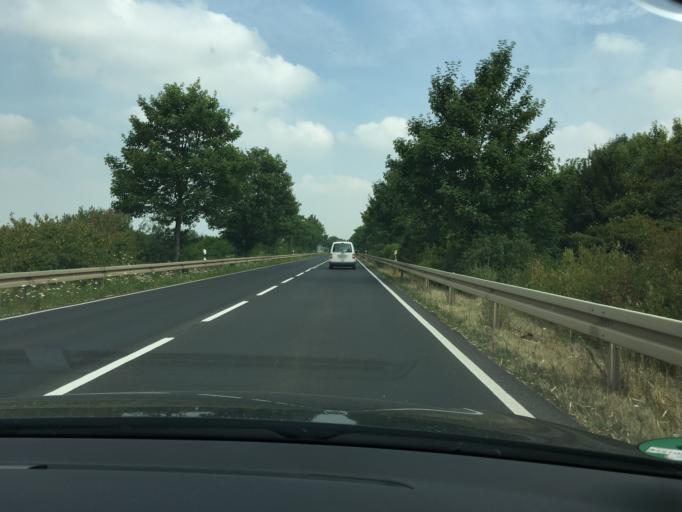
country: DE
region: North Rhine-Westphalia
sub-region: Regierungsbezirk Koln
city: Bergheim
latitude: 50.9260
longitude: 6.6137
